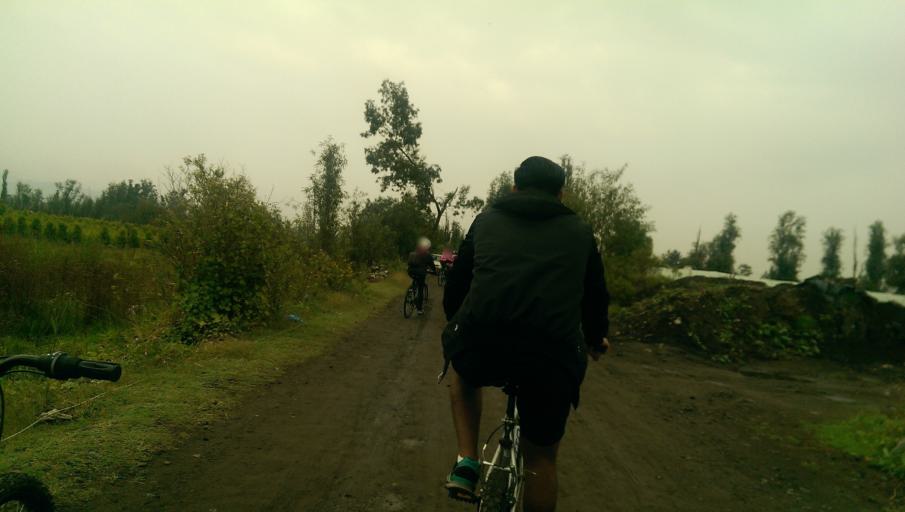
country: MX
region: Mexico City
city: Xochimilco
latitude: 19.2655
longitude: -99.0743
